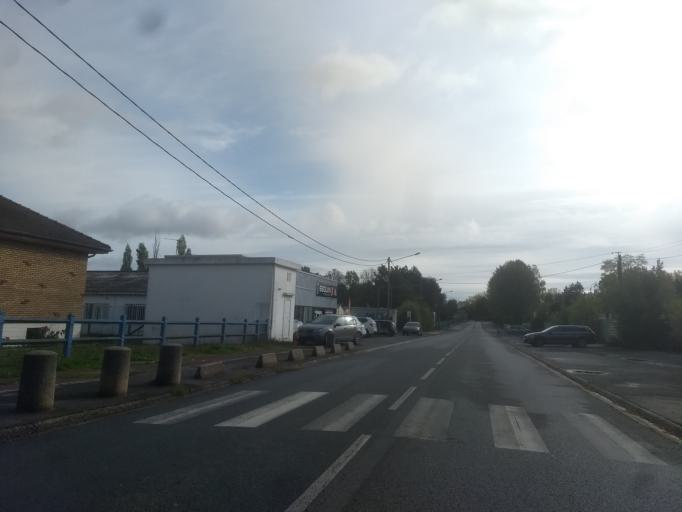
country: FR
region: Nord-Pas-de-Calais
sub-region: Departement du Pas-de-Calais
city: Dainville
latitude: 50.2976
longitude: 2.7316
